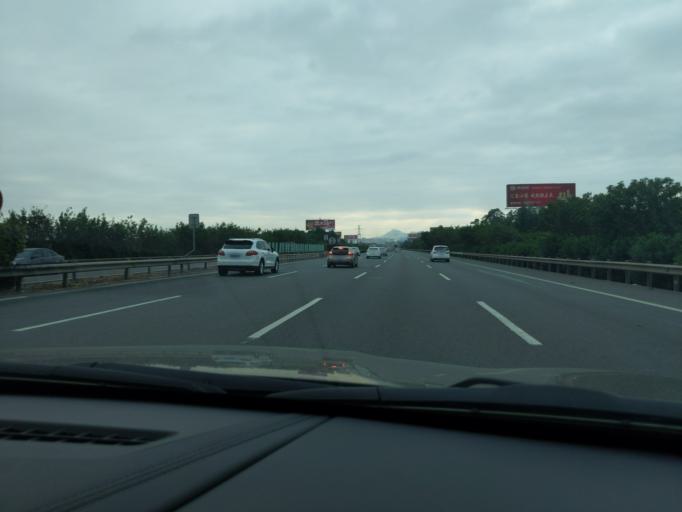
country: CN
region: Fujian
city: Neikeng
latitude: 24.7700
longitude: 118.4526
